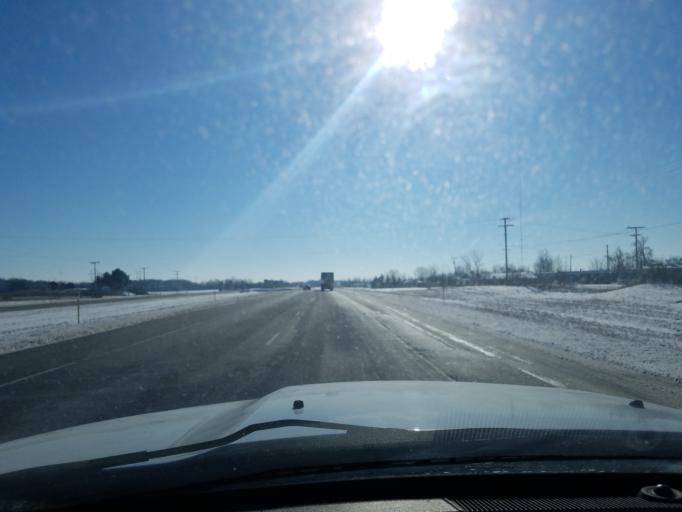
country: US
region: Indiana
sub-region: Noble County
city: Kendallville
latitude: 41.4033
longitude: -85.2534
